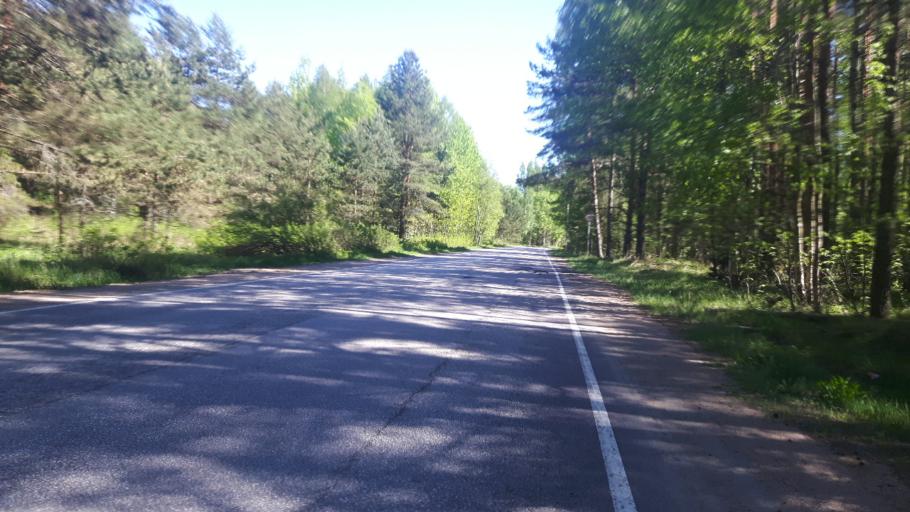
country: RU
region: Leningrad
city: Glebychevo
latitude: 60.2871
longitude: 28.8749
